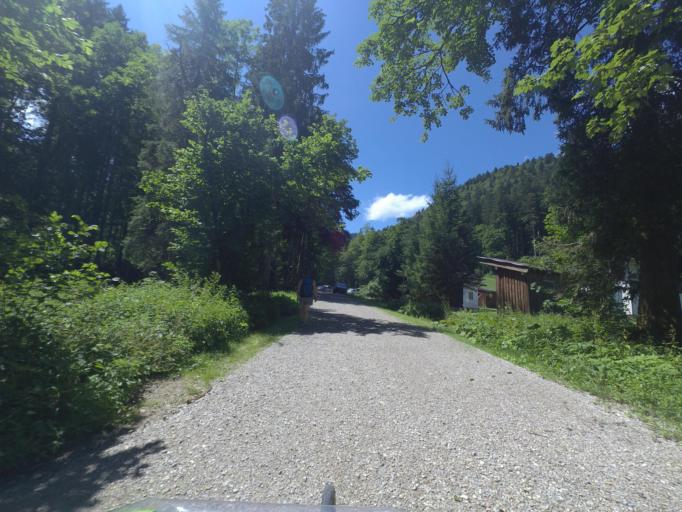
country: AT
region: Salzburg
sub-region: Politischer Bezirk Salzburg-Umgebung
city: Hintersee
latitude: 47.7089
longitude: 13.2854
